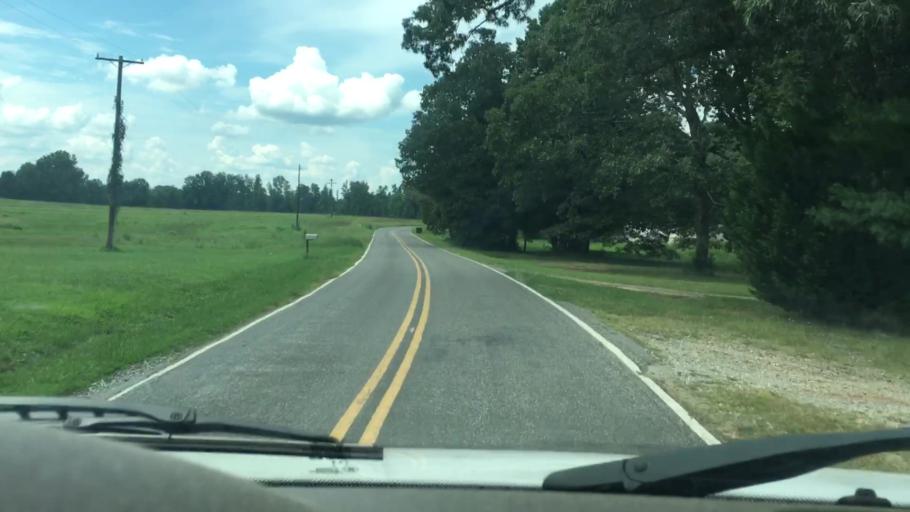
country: US
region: North Carolina
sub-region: Iredell County
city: Troutman
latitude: 35.6719
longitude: -80.8384
